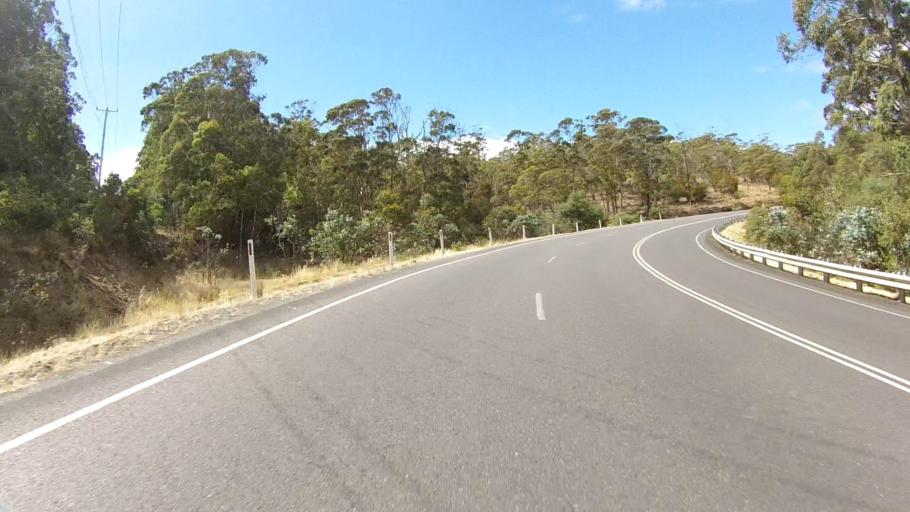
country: AU
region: Tasmania
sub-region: Sorell
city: Sorell
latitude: -42.6321
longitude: 147.6189
